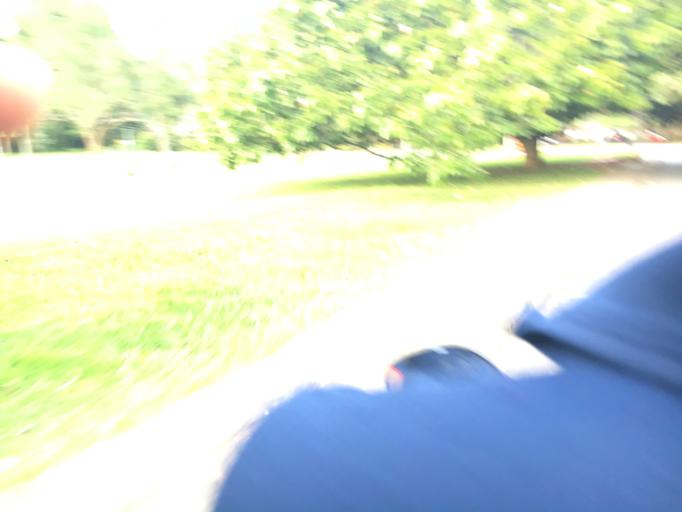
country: LK
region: Central
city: Kandy
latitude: 7.2552
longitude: 80.5989
